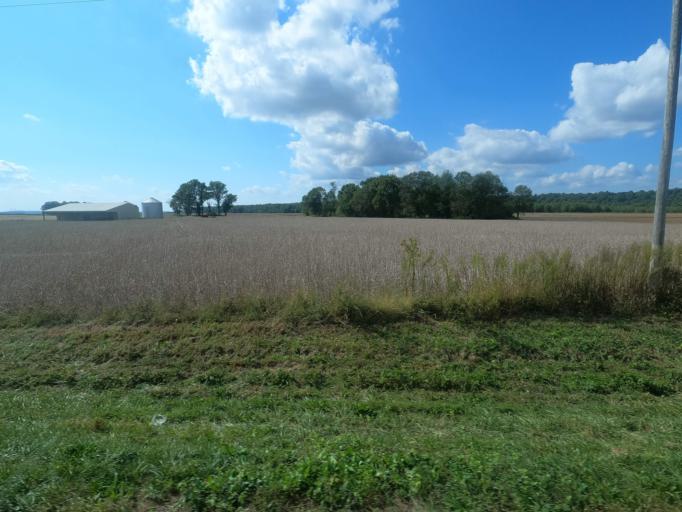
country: US
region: Illinois
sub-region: Massac County
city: Metropolis
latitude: 37.2927
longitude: -88.7563
